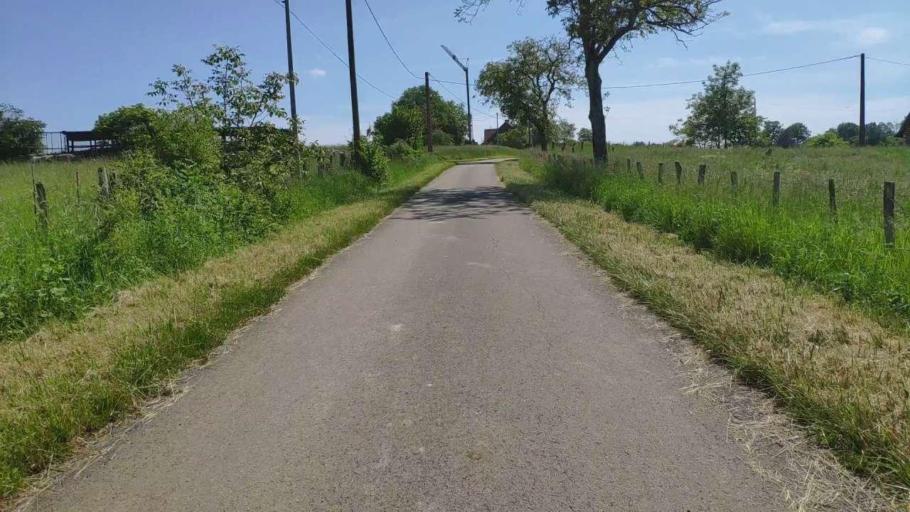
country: FR
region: Franche-Comte
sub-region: Departement du Jura
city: Bletterans
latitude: 46.7923
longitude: 5.4151
